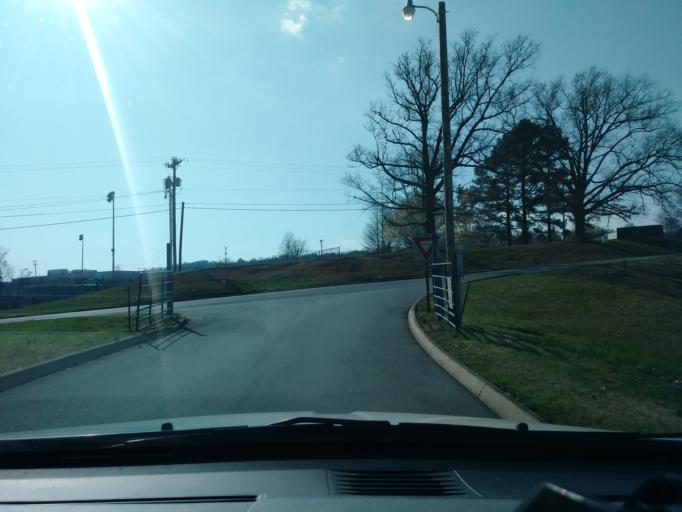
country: US
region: Tennessee
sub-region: Greene County
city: Greeneville
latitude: 36.1485
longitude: -82.8421
